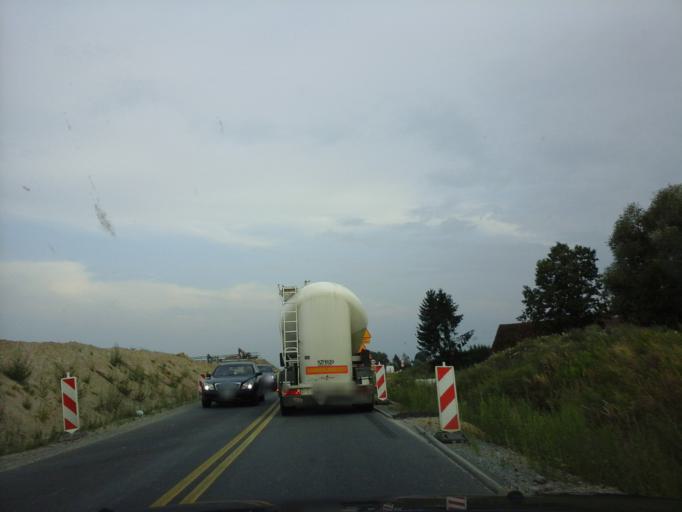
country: PL
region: Lower Silesian Voivodeship
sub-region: Powiat trzebnicki
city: Zmigrod
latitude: 51.5122
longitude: 16.8917
